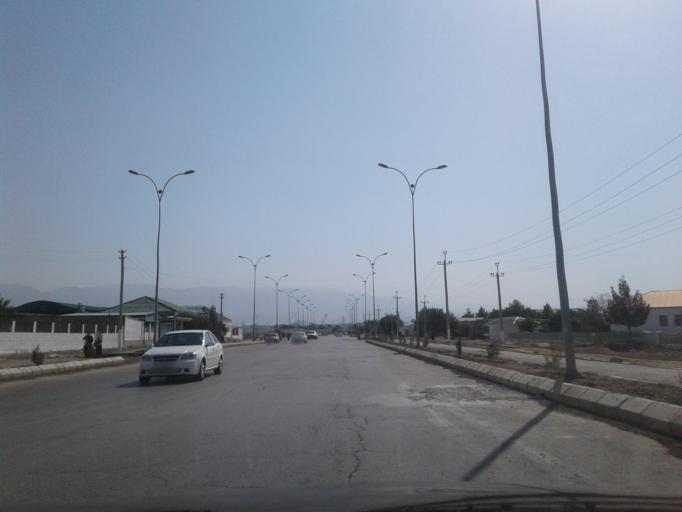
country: TM
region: Ahal
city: Ashgabat
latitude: 37.9716
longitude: 58.4263
